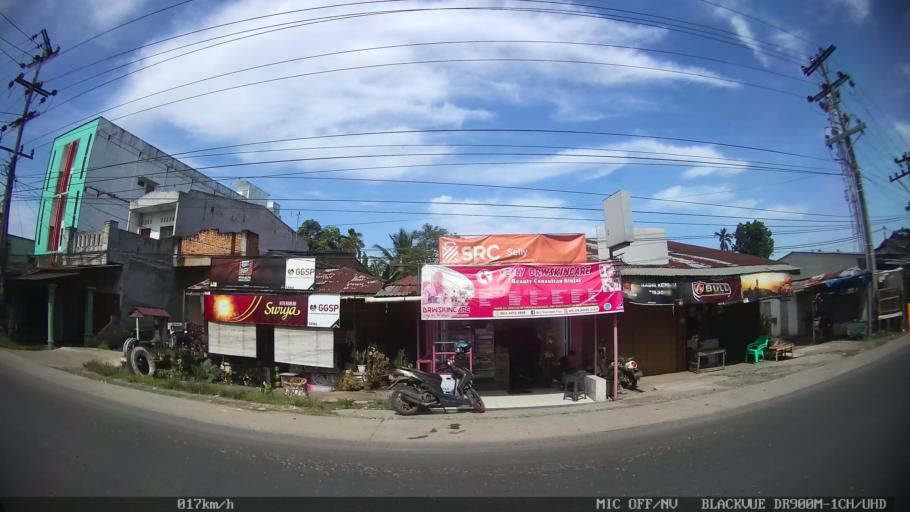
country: ID
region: North Sumatra
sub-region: Kabupaten Langkat
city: Stabat
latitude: 3.7020
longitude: 98.5065
